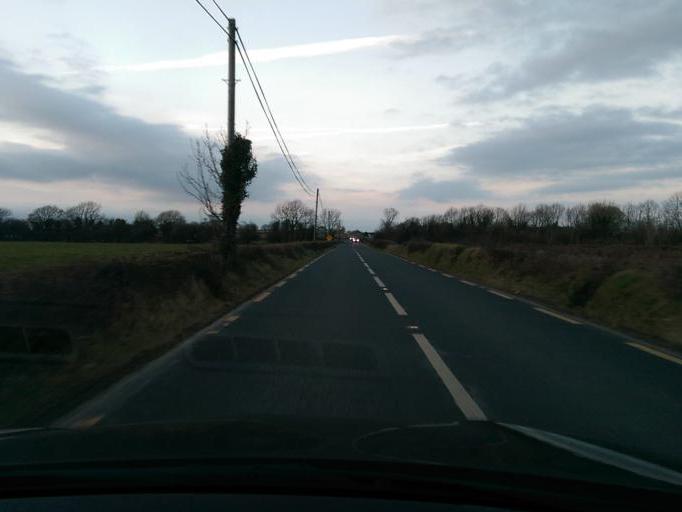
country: IE
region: Connaught
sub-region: County Galway
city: Portumna
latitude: 53.0082
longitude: -8.1254
